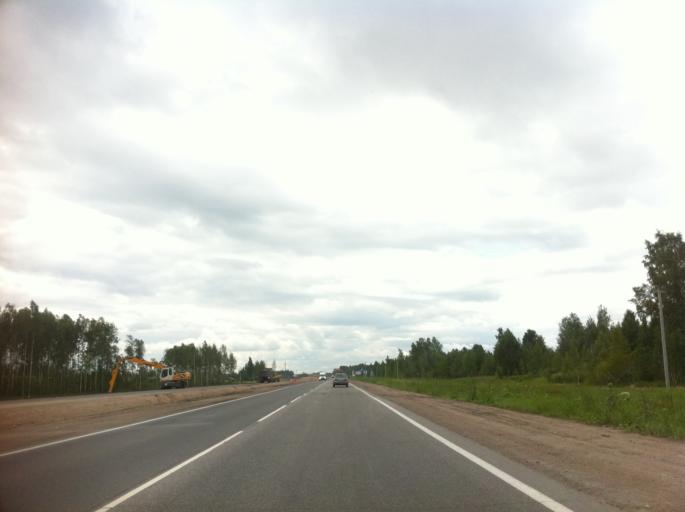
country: RU
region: Leningrad
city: Gatchina
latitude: 59.5690
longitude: 30.1684
